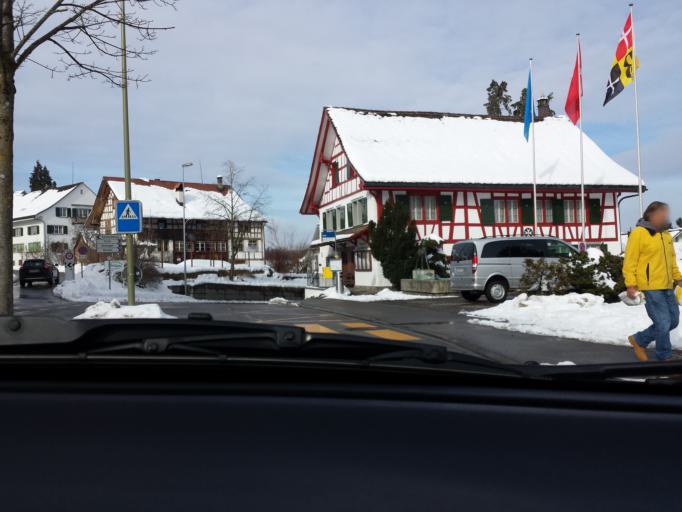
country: CH
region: Zurich
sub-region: Bezirk Hinwil
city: Bubikon
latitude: 47.2685
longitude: 8.8193
